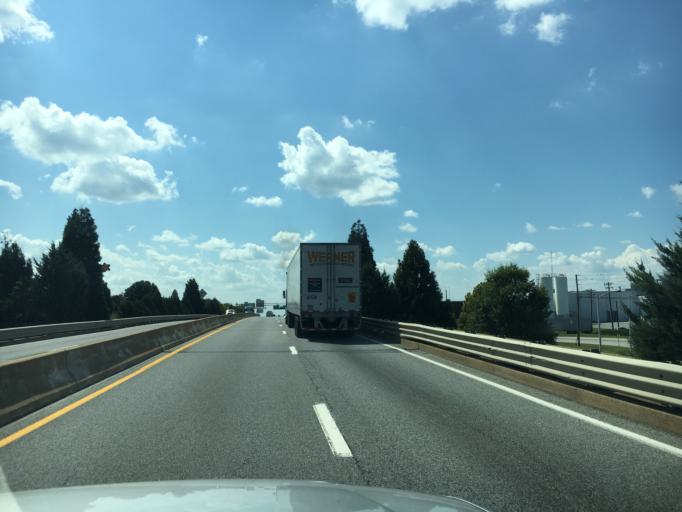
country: US
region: South Carolina
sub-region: Spartanburg County
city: Southern Shops
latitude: 34.9848
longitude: -81.9717
